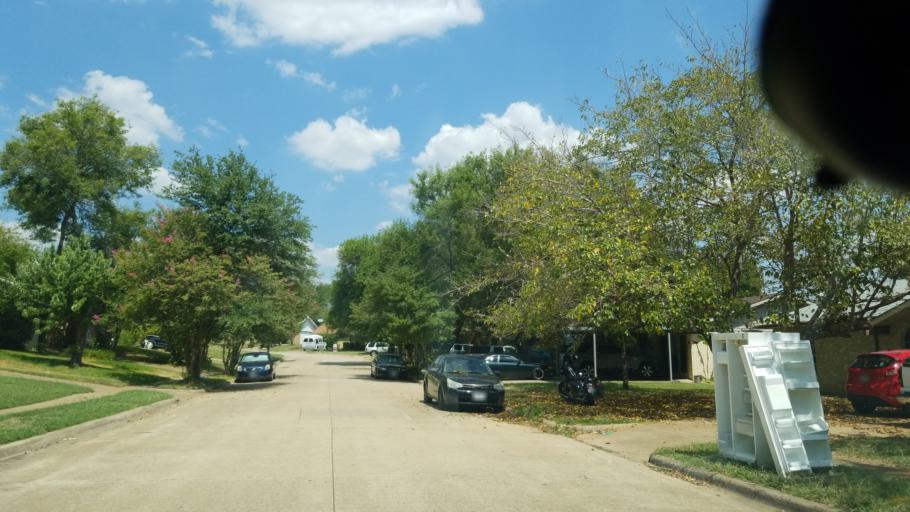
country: US
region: Texas
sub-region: Dallas County
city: Grand Prairie
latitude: 32.7043
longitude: -96.9870
